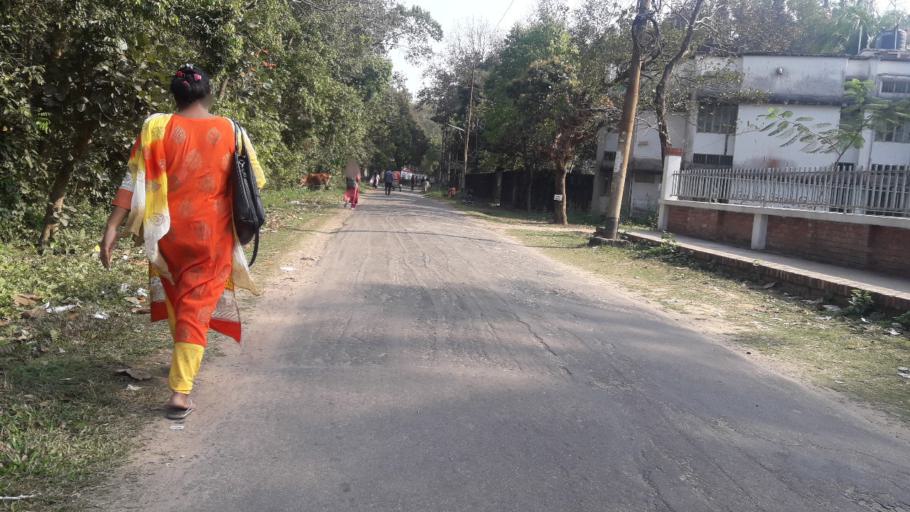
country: BD
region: Chittagong
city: Chittagong
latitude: 22.4690
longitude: 91.7879
